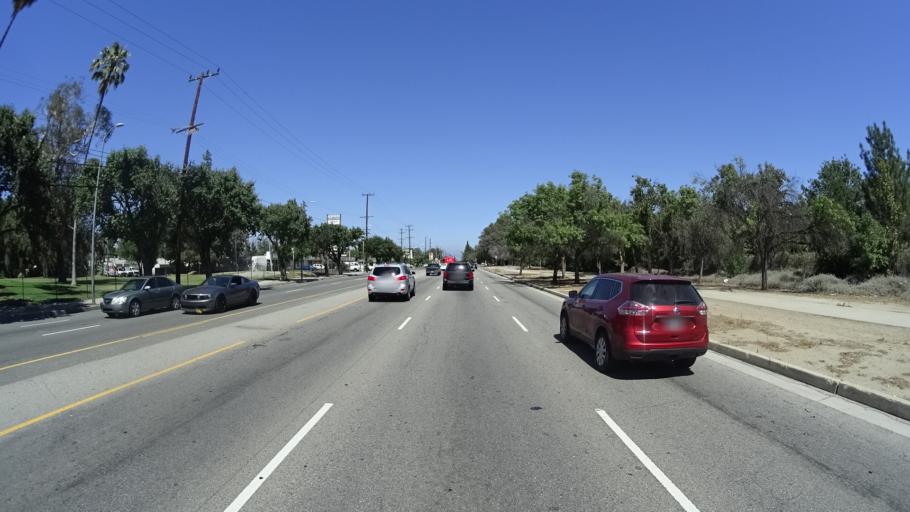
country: US
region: California
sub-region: Los Angeles County
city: Van Nuys
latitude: 34.1866
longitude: -118.4878
